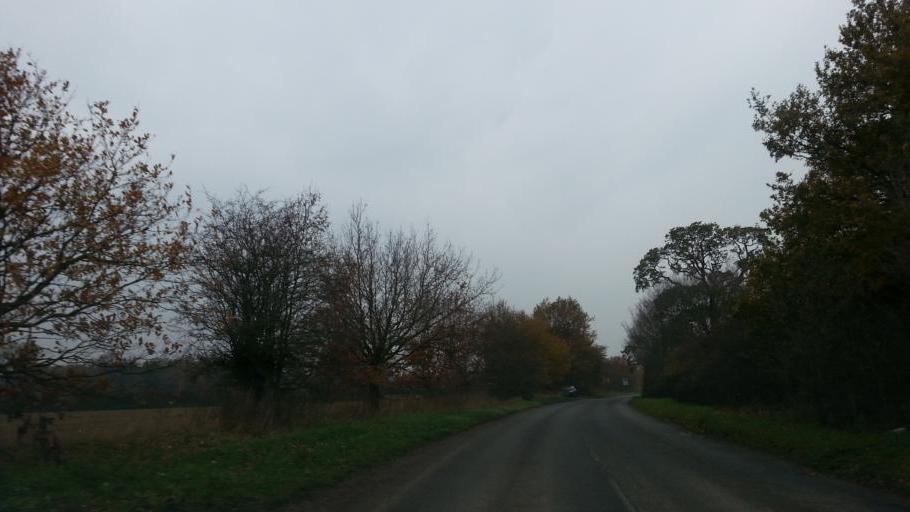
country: GB
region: England
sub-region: Suffolk
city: Thurston
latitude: 52.2318
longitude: 0.8090
